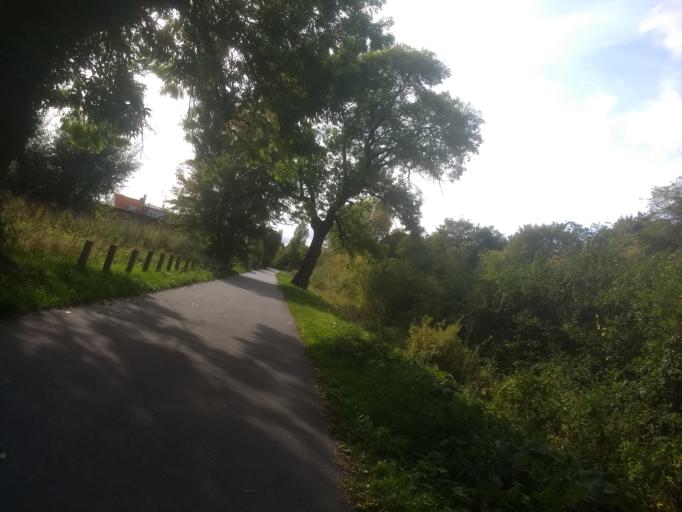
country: FR
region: Nord-Pas-de-Calais
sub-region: Departement du Pas-de-Calais
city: Achicourt
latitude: 50.2794
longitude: 2.7604
